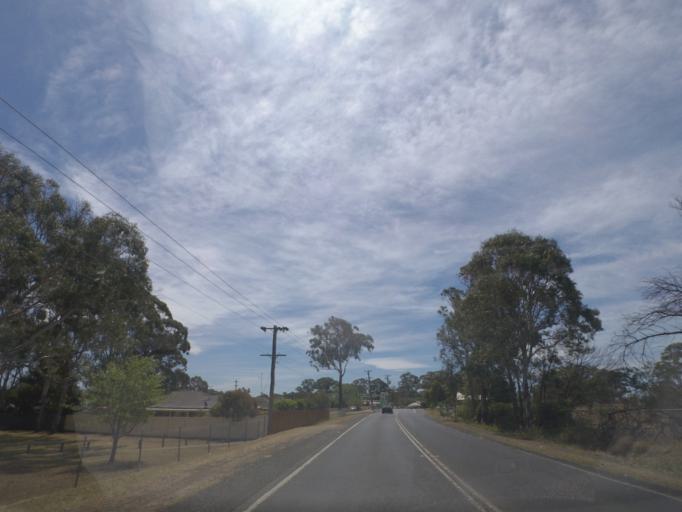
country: AU
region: New South Wales
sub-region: Wollondilly
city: Buxton
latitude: -34.2940
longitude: 150.5812
